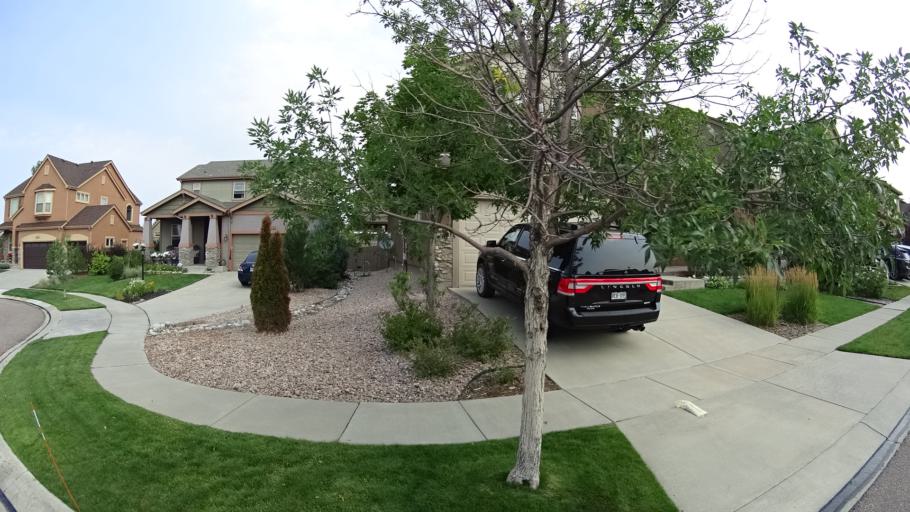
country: US
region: Colorado
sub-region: El Paso County
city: Black Forest
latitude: 38.9686
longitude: -104.7370
